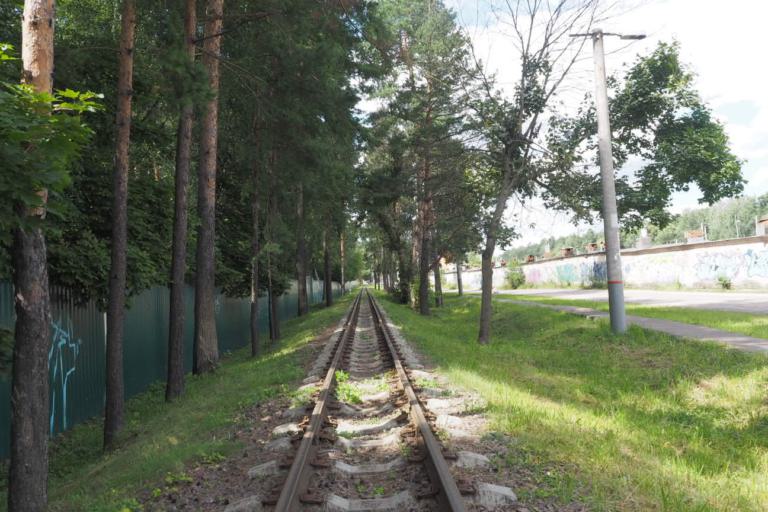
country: RU
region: Moskovskaya
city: Zhukovskiy
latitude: 55.5985
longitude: 38.1423
